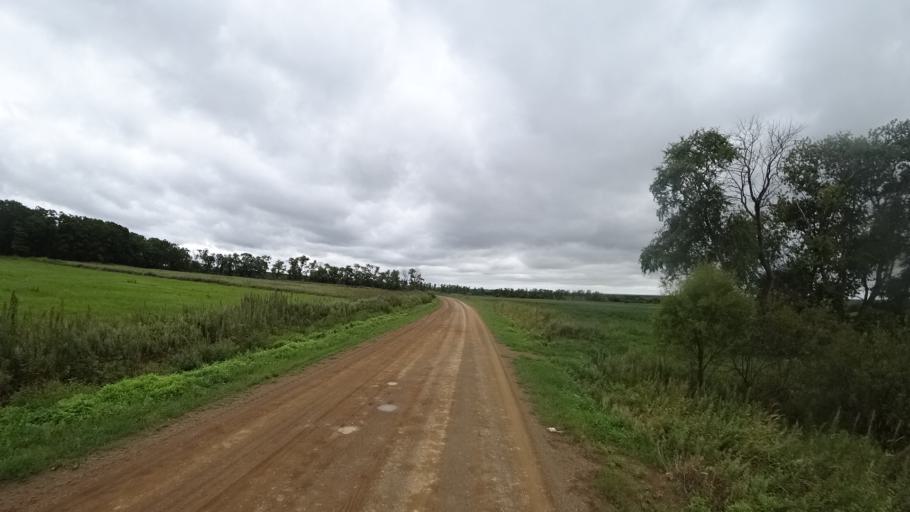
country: RU
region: Primorskiy
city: Chernigovka
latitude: 44.4496
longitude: 132.5766
